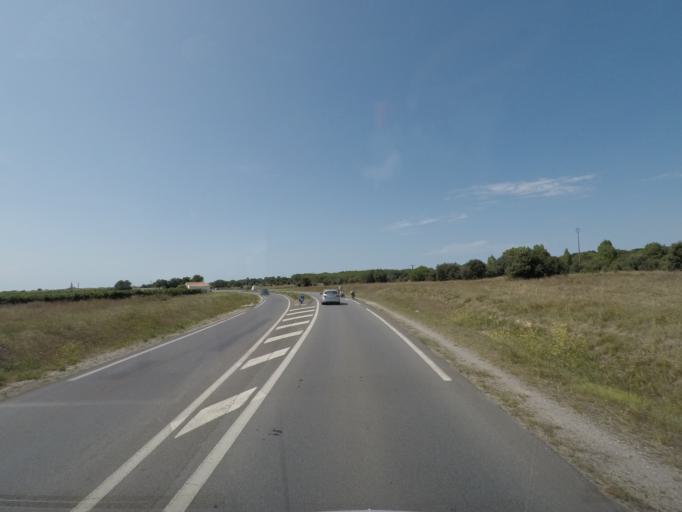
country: FR
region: Poitou-Charentes
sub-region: Departement de la Charente-Maritime
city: Rivedoux-Plage
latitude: 46.1540
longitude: -1.2899
